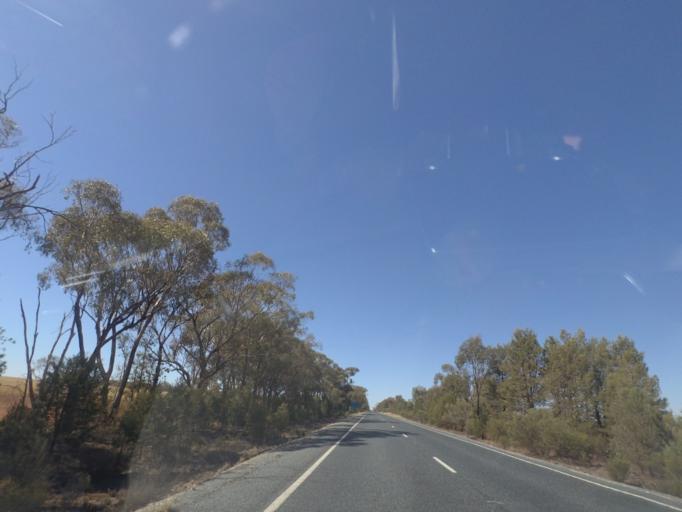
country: AU
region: New South Wales
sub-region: Bland
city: West Wyalong
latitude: -34.1556
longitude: 147.1177
